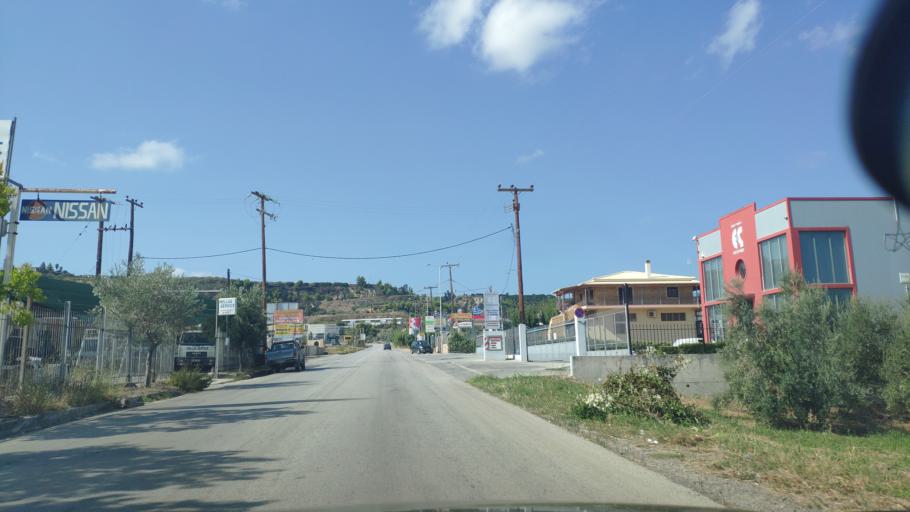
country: GR
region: Peloponnese
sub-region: Nomos Korinthias
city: Moulki
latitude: 38.0029
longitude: 22.7223
